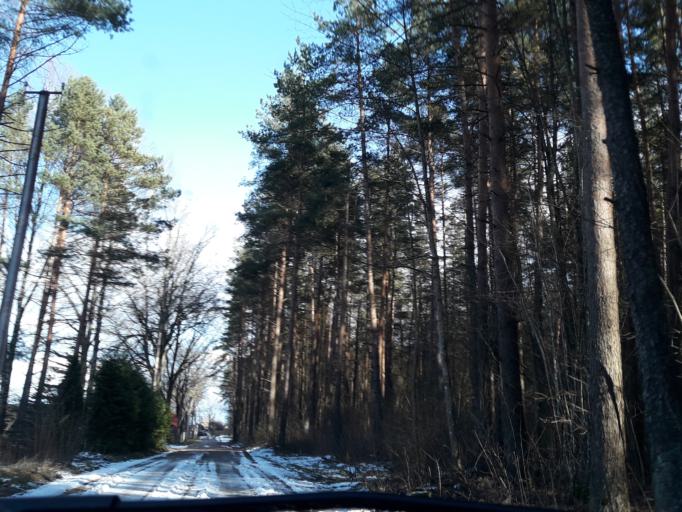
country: LV
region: Kekava
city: Kekava
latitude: 56.8475
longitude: 24.1854
